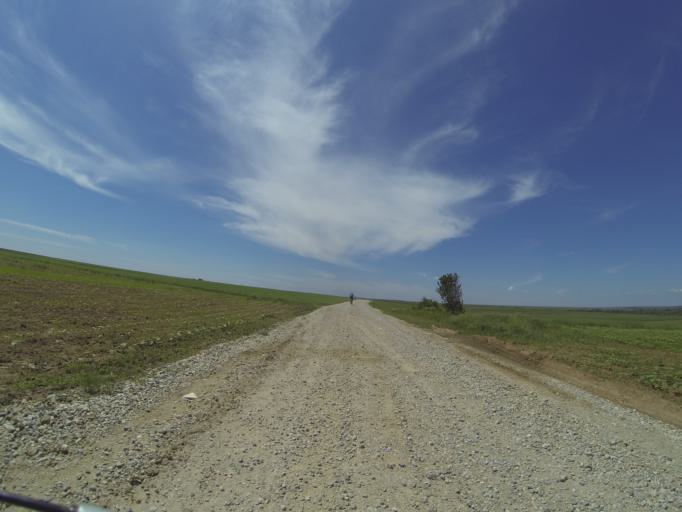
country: RO
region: Dolj
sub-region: Comuna Teslui
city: Teslui
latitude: 44.1896
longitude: 24.1630
